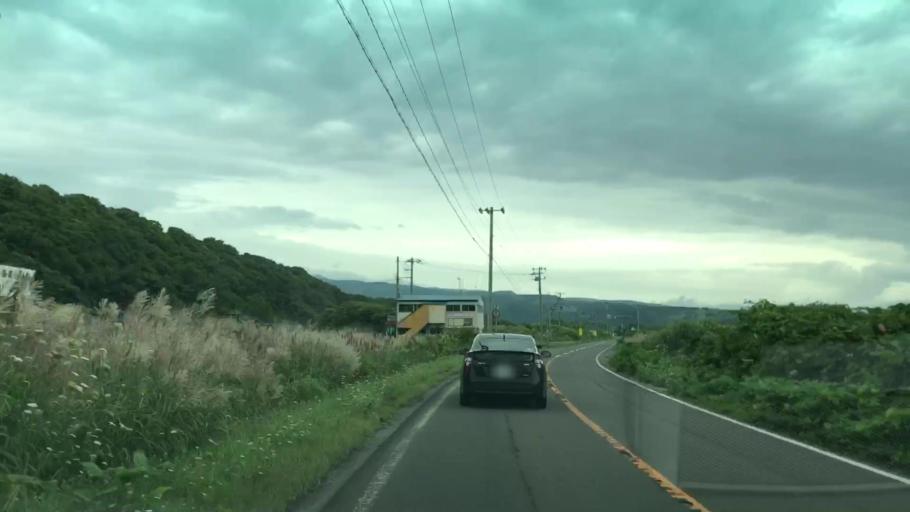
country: JP
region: Hokkaido
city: Iwanai
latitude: 42.8962
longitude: 140.3778
